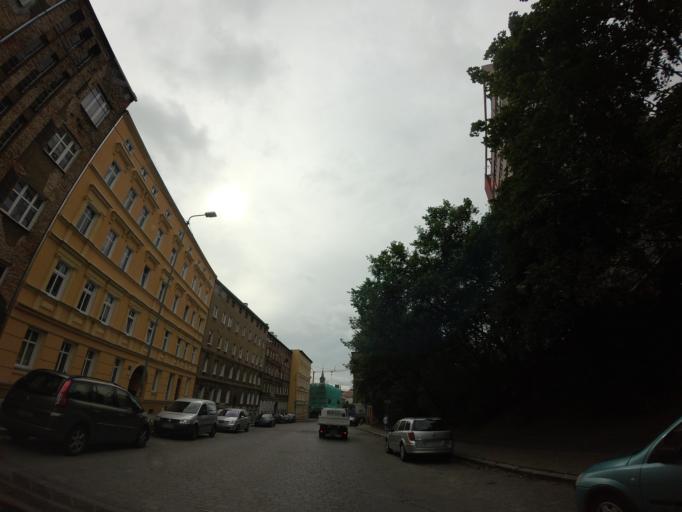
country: PL
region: West Pomeranian Voivodeship
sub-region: Szczecin
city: Szczecin
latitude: 53.4473
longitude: 14.5447
